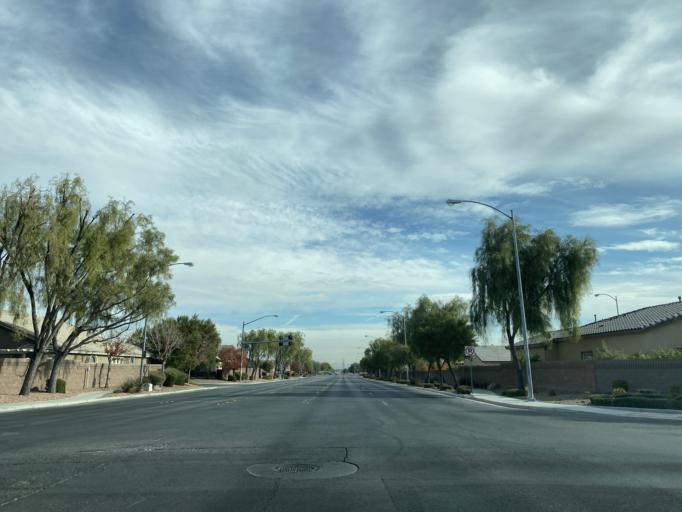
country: US
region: Nevada
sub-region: Clark County
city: North Las Vegas
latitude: 36.2469
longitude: -115.1397
